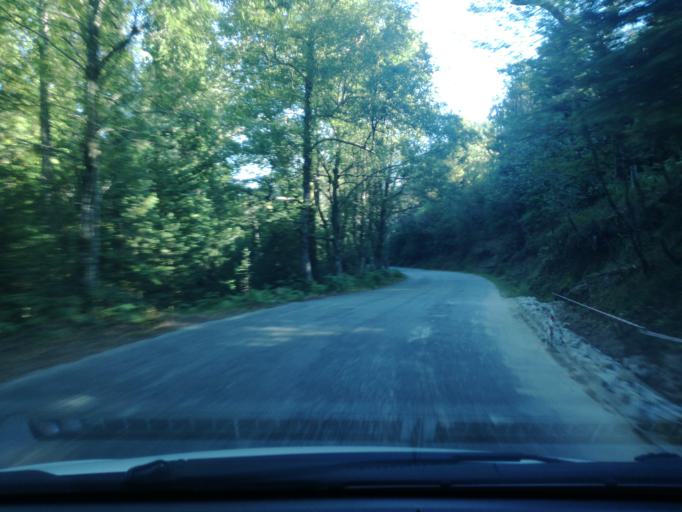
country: ES
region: Galicia
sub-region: Provincia de Ourense
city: Lobios
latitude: 41.7713
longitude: -8.1445
